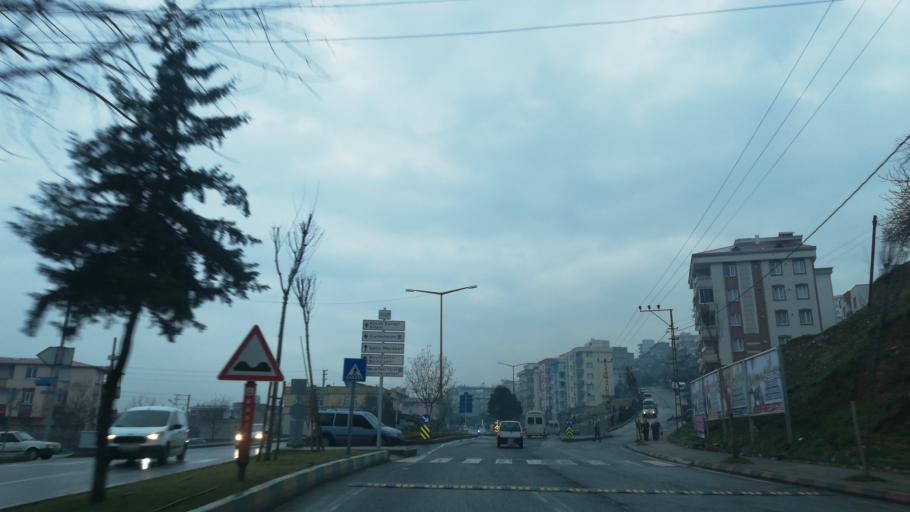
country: TR
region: Kahramanmaras
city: Kahramanmaras
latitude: 37.5818
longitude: 36.9575
